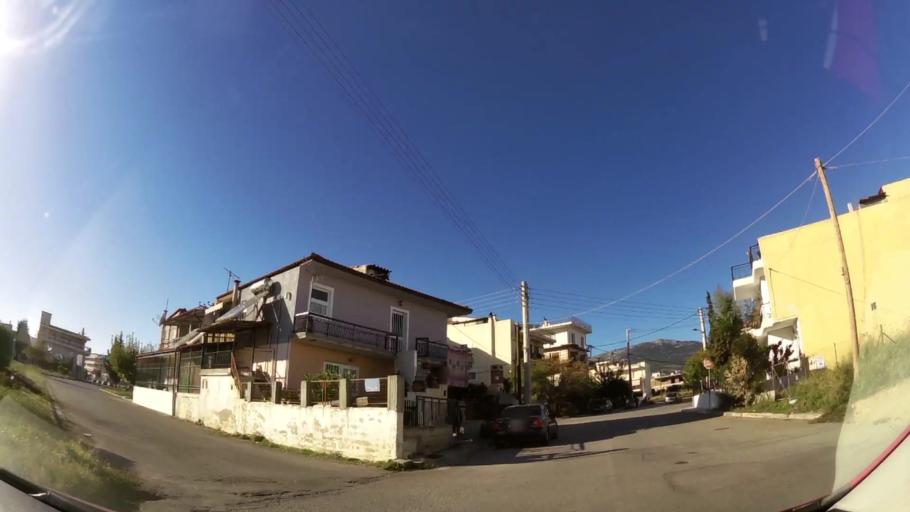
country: GR
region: Attica
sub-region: Nomarchia Anatolikis Attikis
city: Acharnes
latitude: 38.0906
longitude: 23.7290
